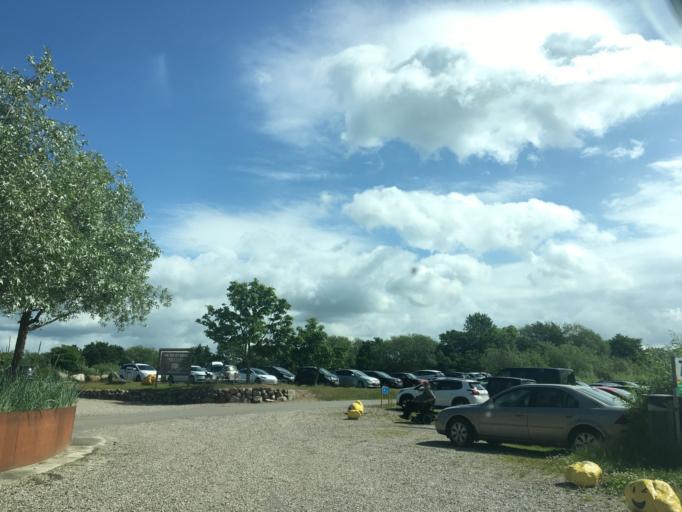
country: DK
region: Zealand
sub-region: Odsherred Kommune
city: Hojby
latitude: 55.8961
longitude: 11.6107
